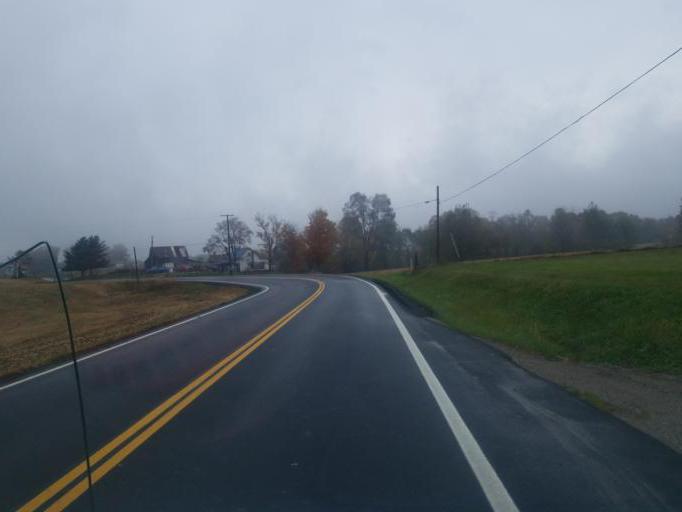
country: US
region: Ohio
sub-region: Morgan County
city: McConnelsville
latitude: 39.5513
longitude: -81.8226
